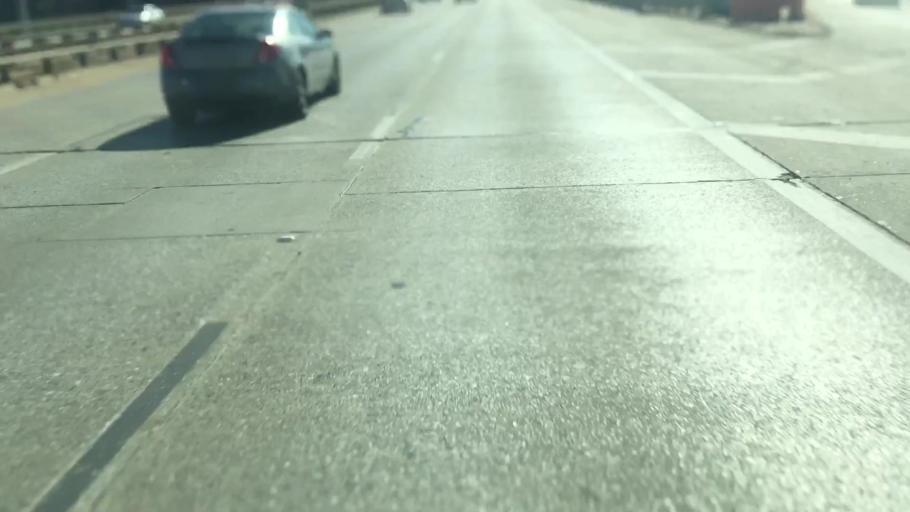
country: US
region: Alabama
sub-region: Jefferson County
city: Birmingham
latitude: 33.5103
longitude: -86.7921
